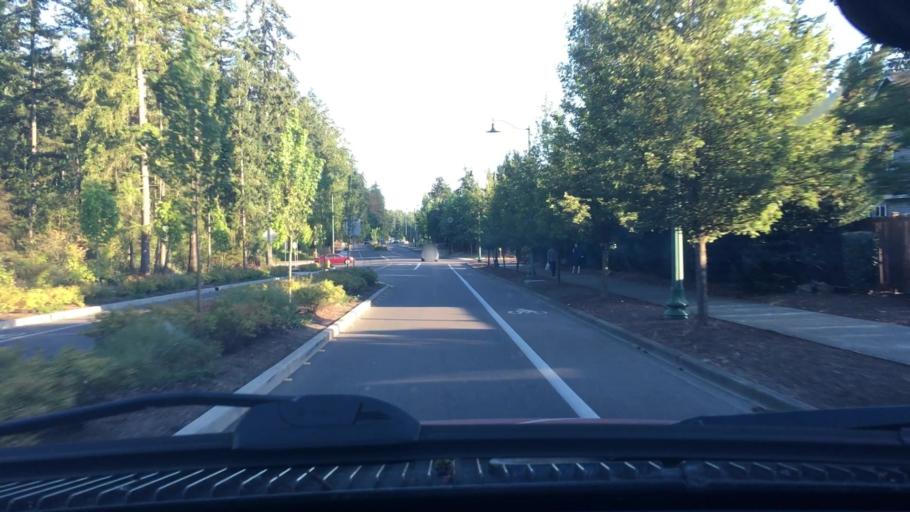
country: US
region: Washington
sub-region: King County
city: Maple Valley
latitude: 47.3554
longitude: -122.0537
